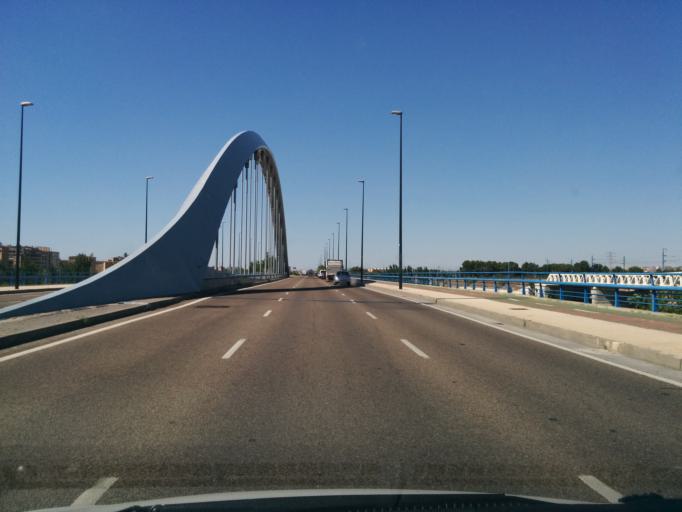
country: ES
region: Aragon
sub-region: Provincia de Zaragoza
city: Zaragoza
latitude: 41.6502
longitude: -0.8548
